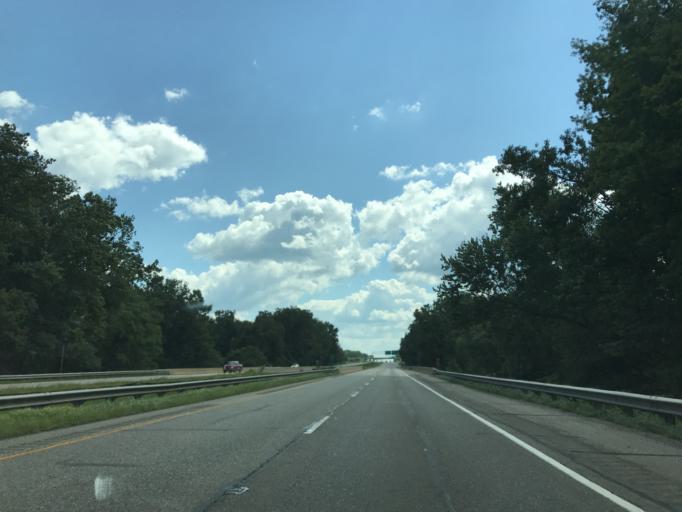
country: US
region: Indiana
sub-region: Marshall County
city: Plymouth
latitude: 41.3555
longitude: -86.2824
